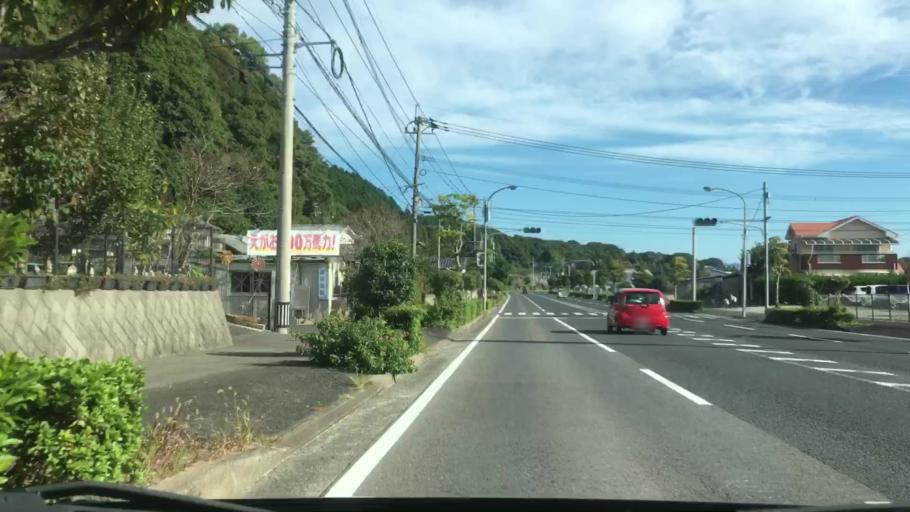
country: JP
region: Nagasaki
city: Sasebo
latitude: 33.1104
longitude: 129.7859
